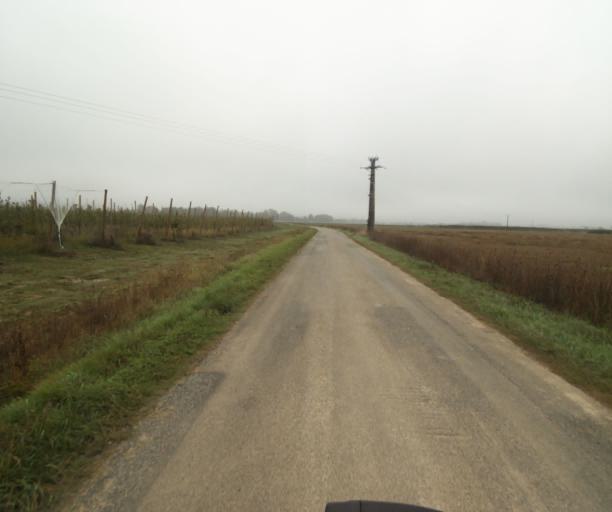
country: FR
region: Midi-Pyrenees
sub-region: Departement du Tarn-et-Garonne
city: Orgueil
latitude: 43.9067
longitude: 1.4234
